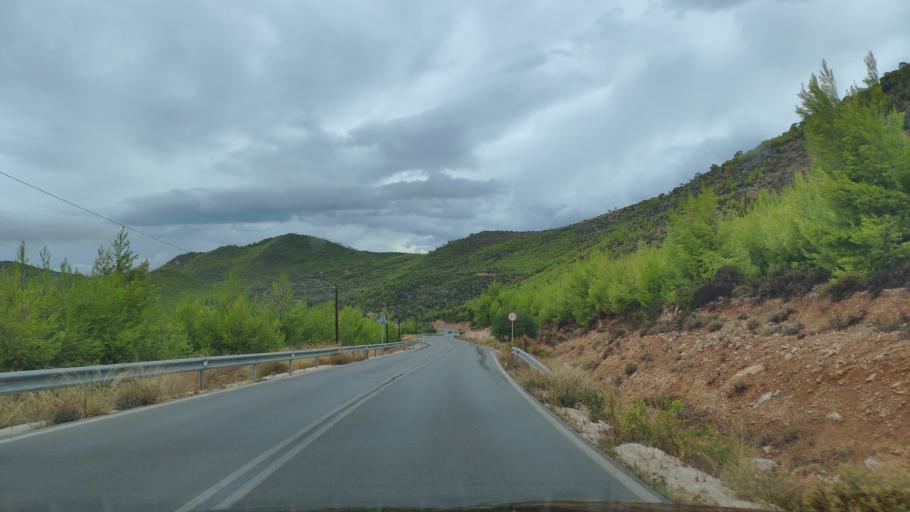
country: GR
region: Peloponnese
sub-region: Nomos Korinthias
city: Perachora
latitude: 38.0305
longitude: 22.9288
